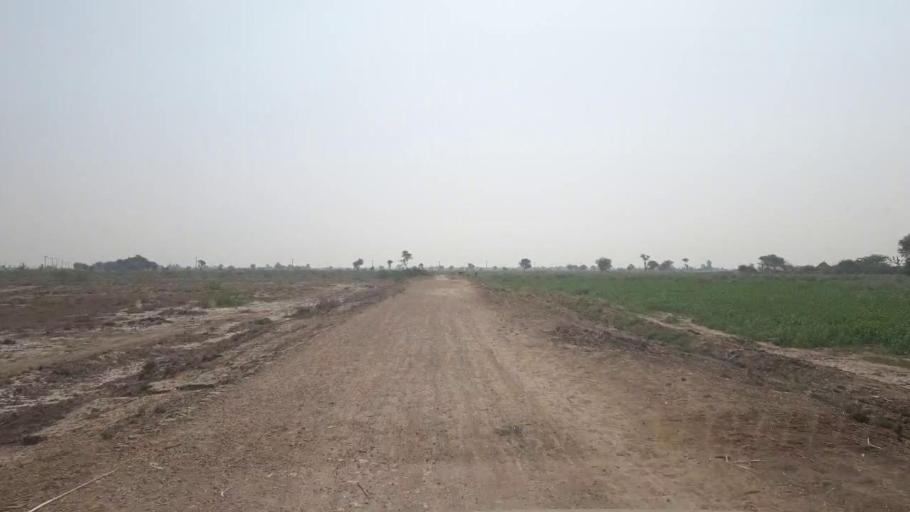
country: PK
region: Sindh
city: Dhoro Naro
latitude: 25.4498
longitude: 69.6215
